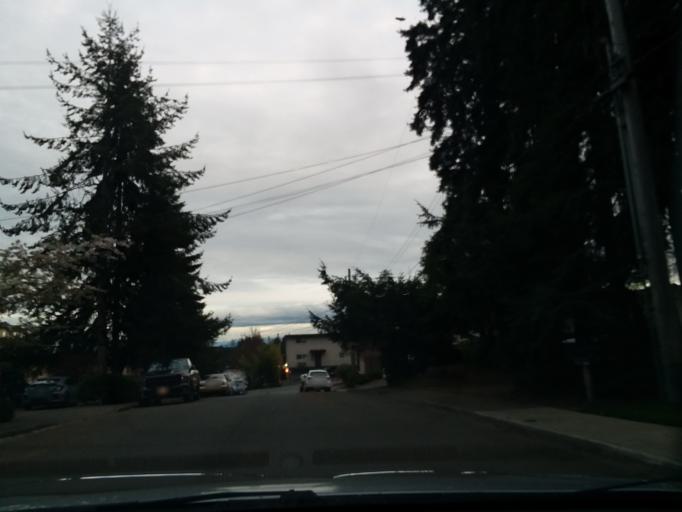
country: US
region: Washington
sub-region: Snohomish County
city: Esperance
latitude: 47.7750
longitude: -122.3483
